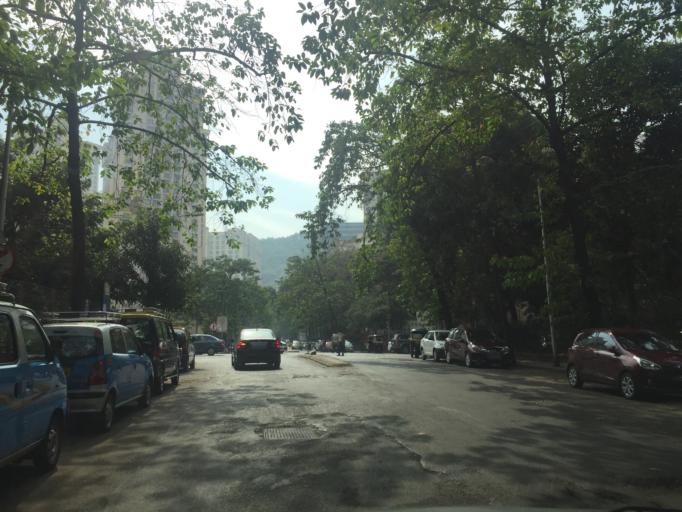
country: IN
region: Maharashtra
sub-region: Mumbai Suburban
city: Powai
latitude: 19.1160
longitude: 72.9081
